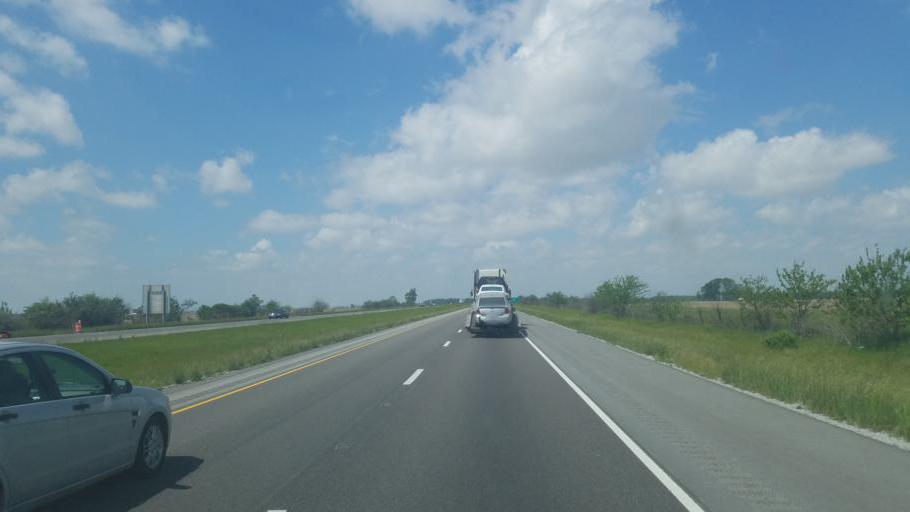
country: US
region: Illinois
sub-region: Clark County
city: Casey
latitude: 39.3178
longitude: -87.9955
